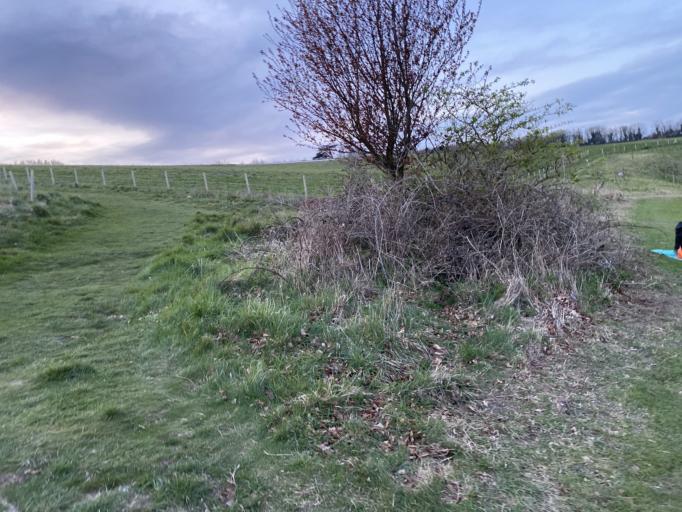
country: GB
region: England
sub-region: Brighton and Hove
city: Brighton
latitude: 50.8707
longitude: -0.0918
